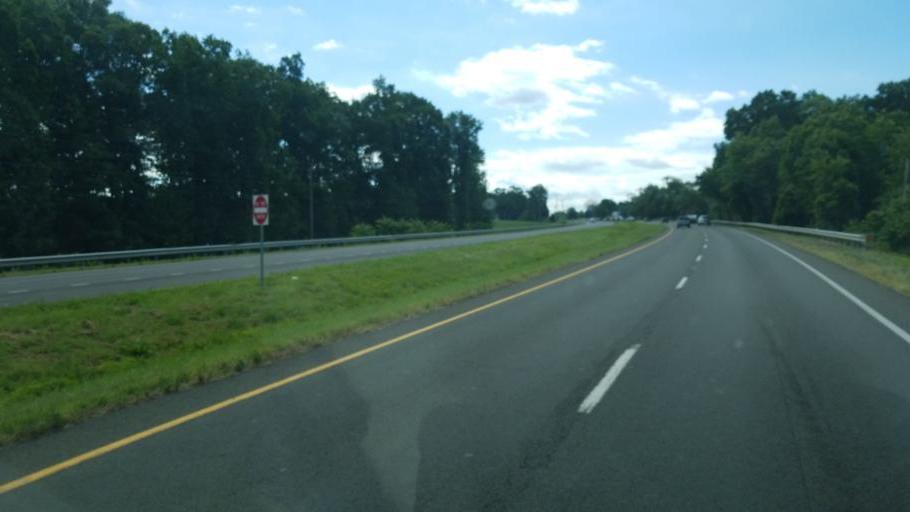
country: US
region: Virginia
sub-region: Fauquier County
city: Bealeton
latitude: 38.5123
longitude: -77.7157
